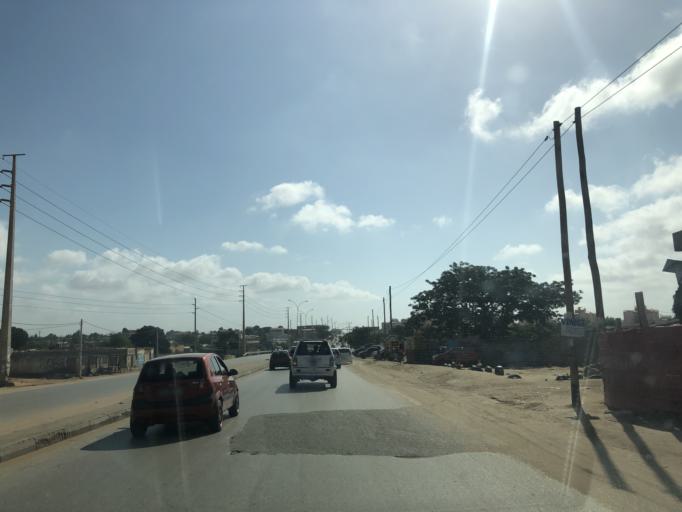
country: AO
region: Luanda
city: Luanda
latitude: -8.9054
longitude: 13.2456
